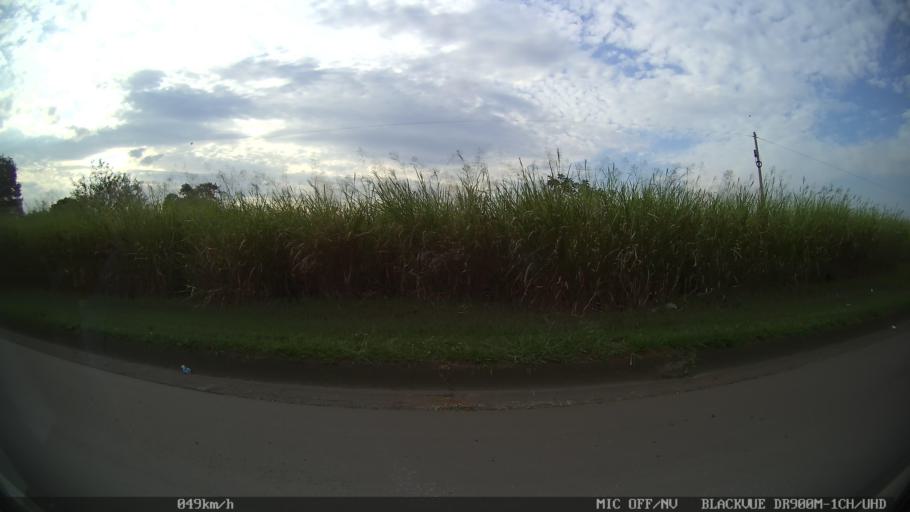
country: BR
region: Sao Paulo
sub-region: Cosmopolis
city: Cosmopolis
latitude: -22.6278
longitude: -47.2715
